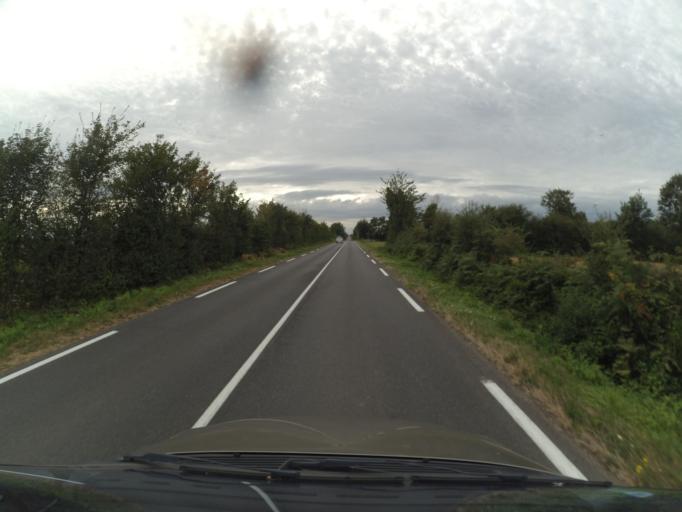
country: FR
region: Pays de la Loire
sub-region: Departement de la Vendee
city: Saint-Aubin-des-Ormeaux
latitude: 47.0197
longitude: -1.0195
